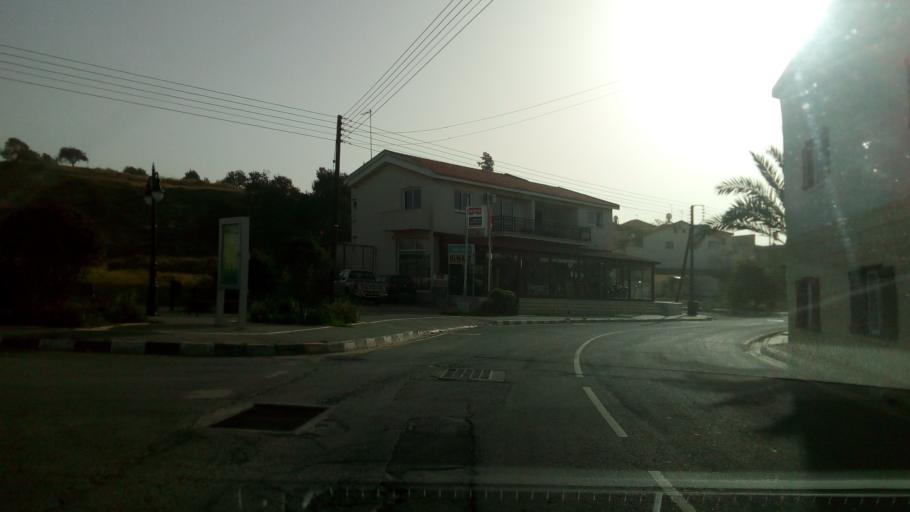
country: CY
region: Larnaka
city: Tersefanou
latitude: 34.8046
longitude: 33.4858
